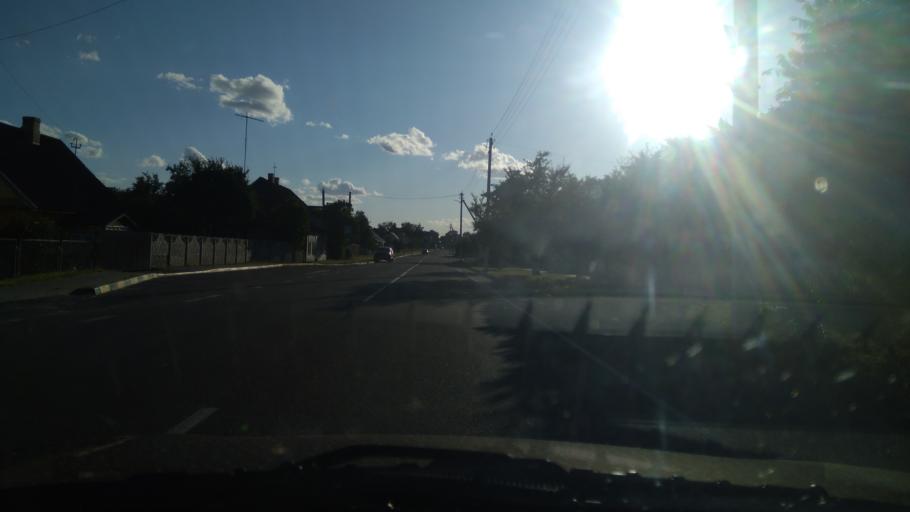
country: BY
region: Brest
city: Pruzhany
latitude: 52.5615
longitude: 24.4731
